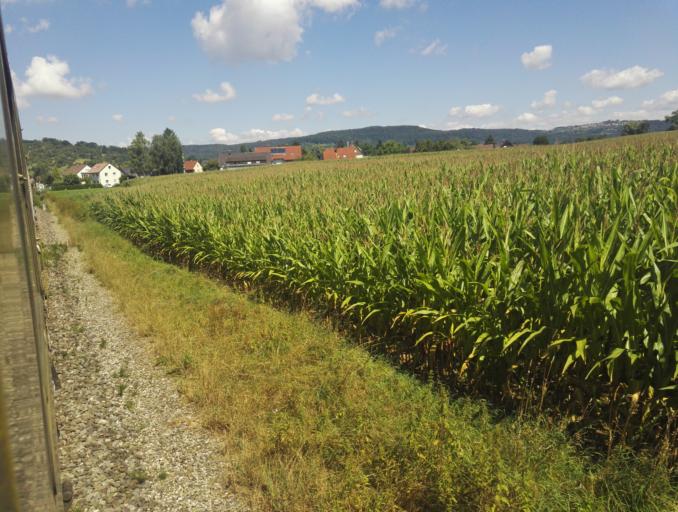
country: DE
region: Baden-Wuerttemberg
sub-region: Regierungsbezirk Stuttgart
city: Rudersberg
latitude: 48.8671
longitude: 9.5305
